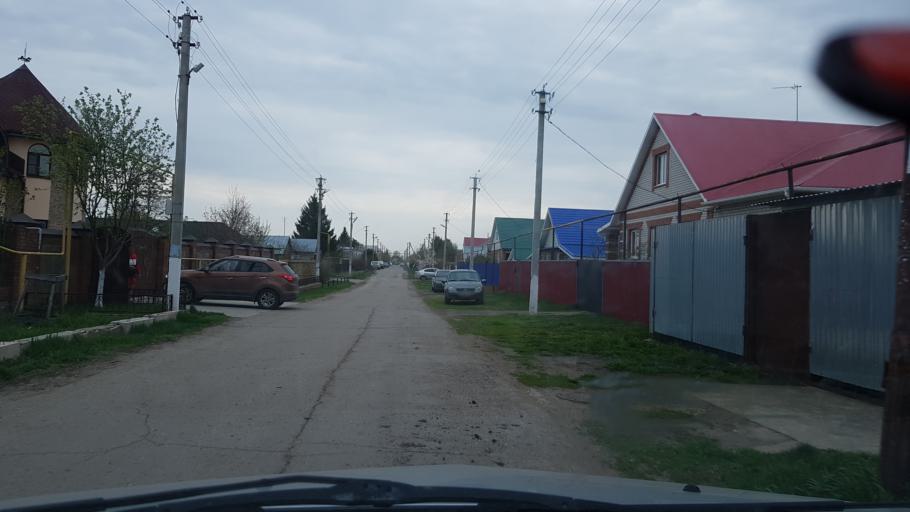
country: RU
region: Samara
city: Khryashchevka
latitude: 53.6715
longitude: 49.0680
